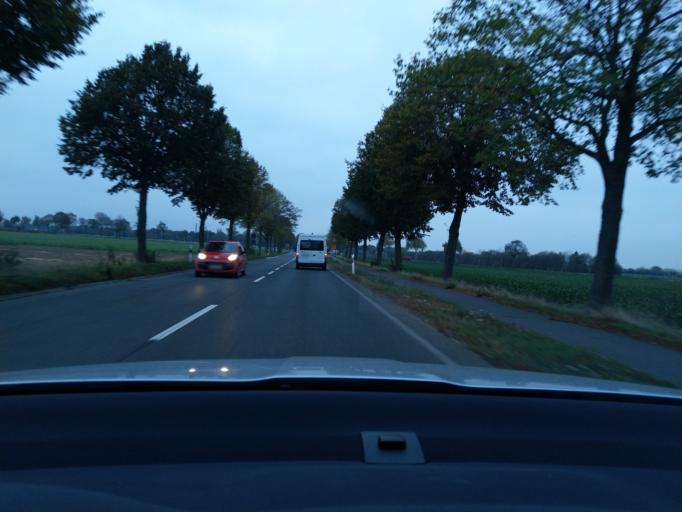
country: DE
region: North Rhine-Westphalia
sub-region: Regierungsbezirk Dusseldorf
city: Schwalmtal
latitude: 51.2285
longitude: 6.2988
